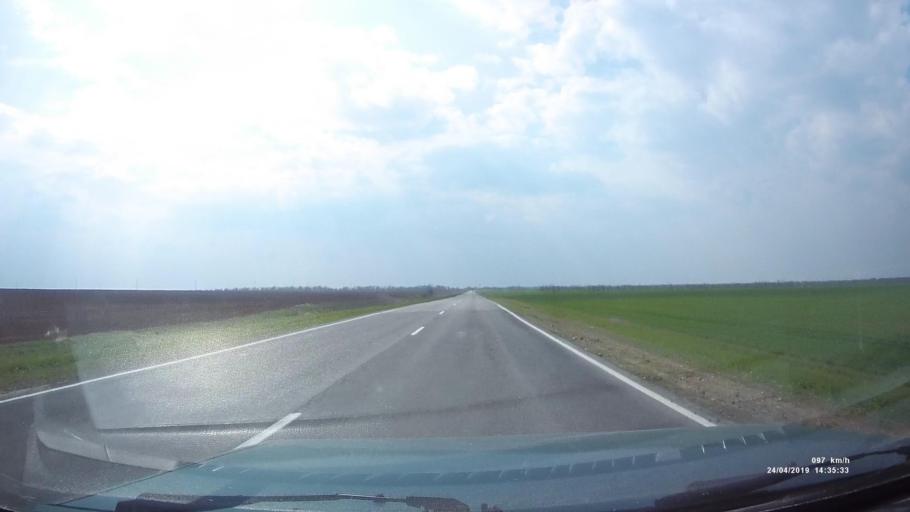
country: RU
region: Rostov
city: Remontnoye
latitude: 46.3739
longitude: 43.9084
